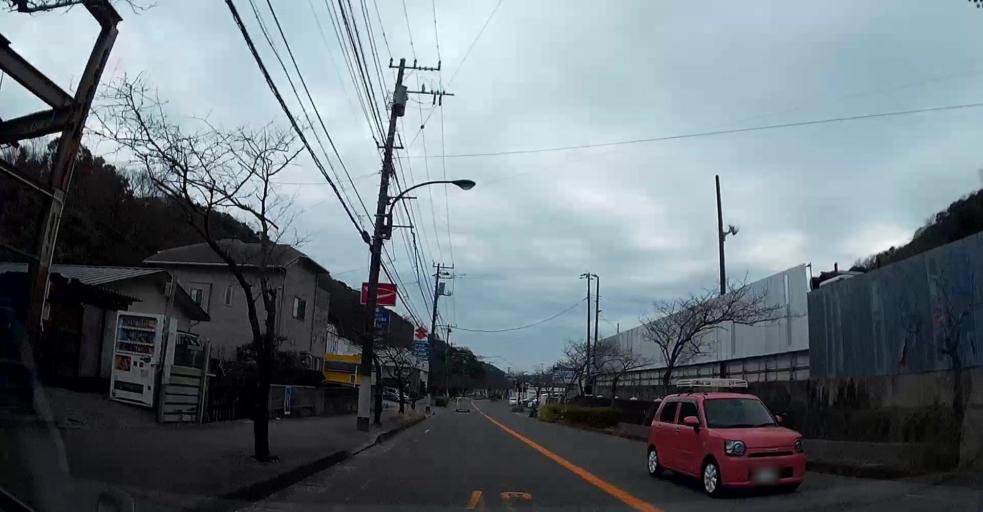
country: JP
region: Kanagawa
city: Yokosuka
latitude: 35.2168
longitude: 139.6730
